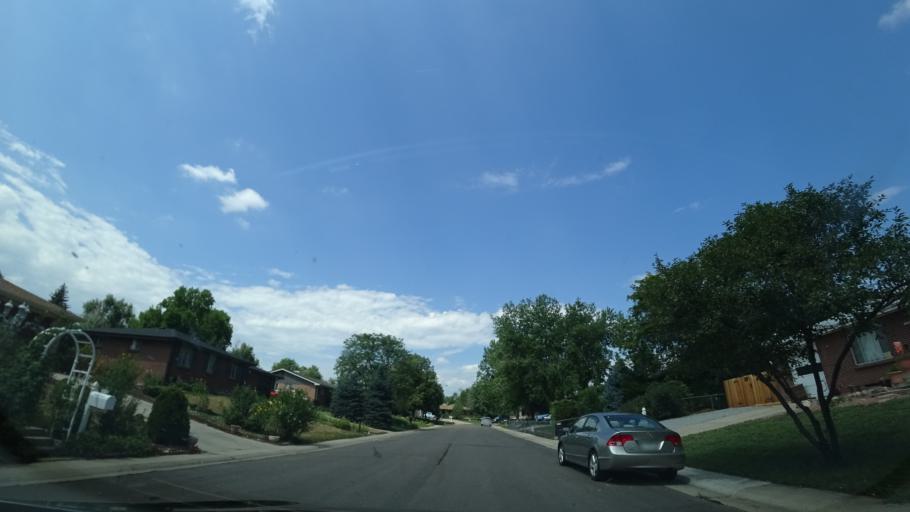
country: US
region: Colorado
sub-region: Jefferson County
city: Lakewood
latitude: 39.7156
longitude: -105.0726
